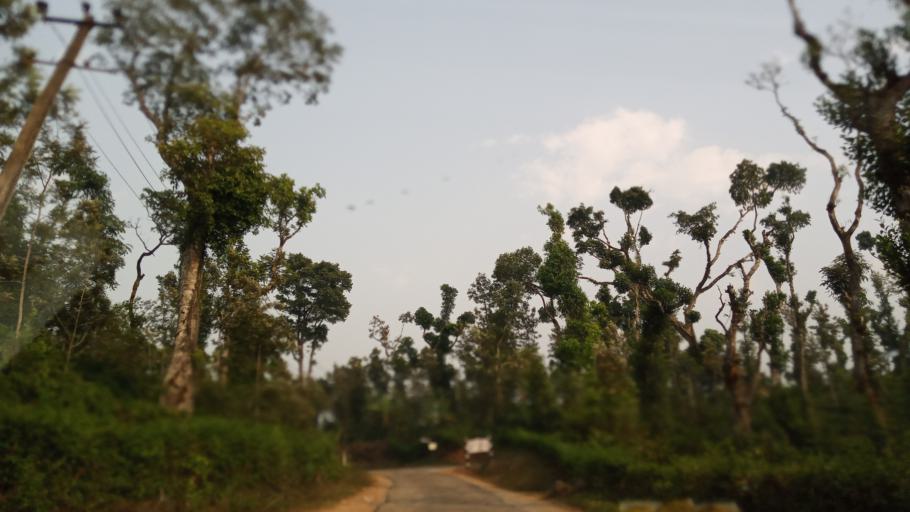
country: IN
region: Karnataka
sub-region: Chikmagalur
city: Mudigere
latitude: 13.0206
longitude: 75.6319
